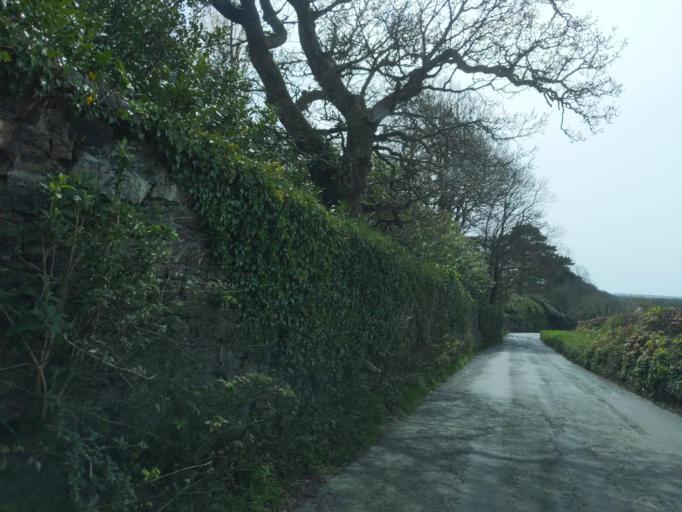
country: GB
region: England
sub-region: Devon
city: Yealmpton
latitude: 50.3994
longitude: -4.0040
